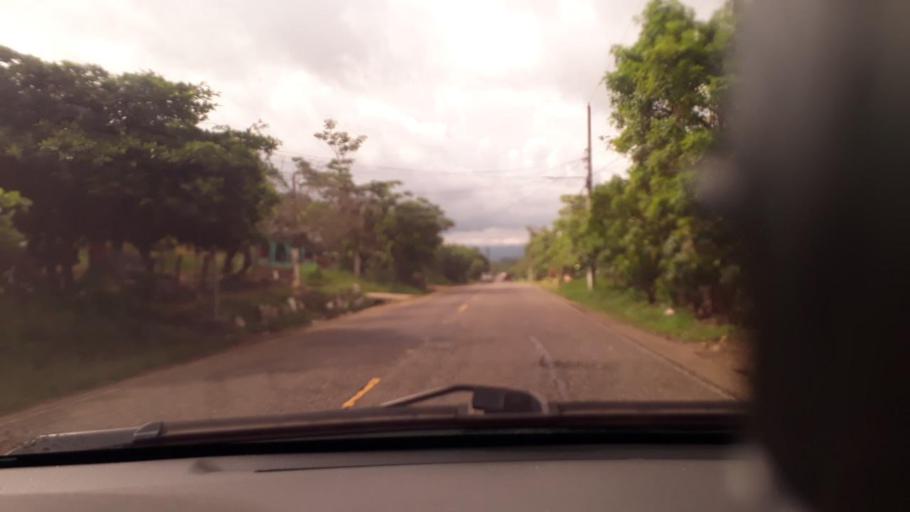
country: GT
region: Jutiapa
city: Quesada
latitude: 14.2126
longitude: -90.0240
